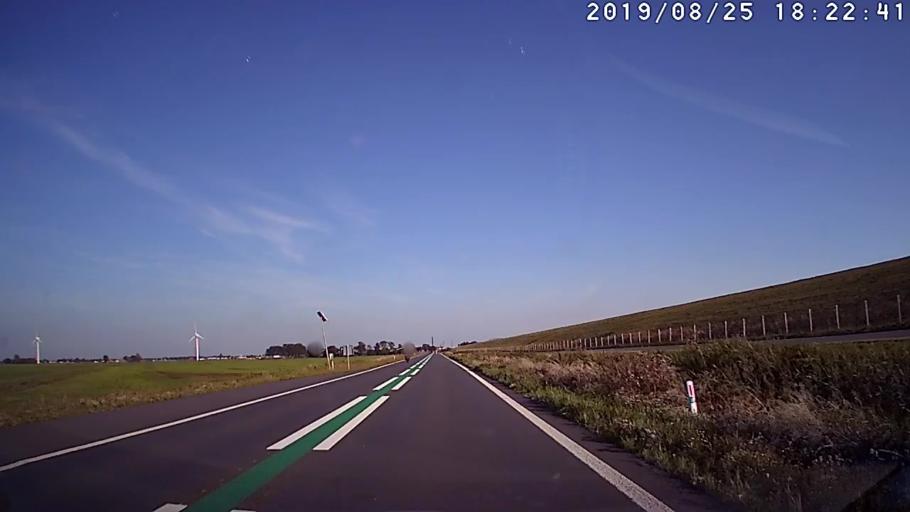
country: NL
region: Friesland
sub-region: Gemeente Lemsterland
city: Lemmer
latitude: 52.8631
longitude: 5.6528
